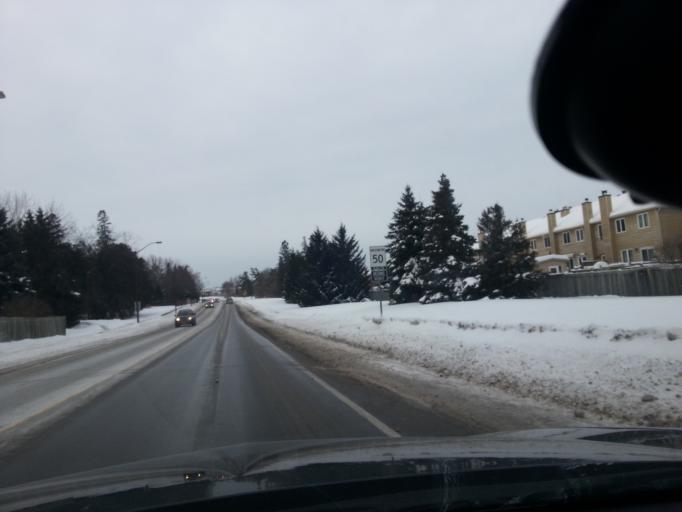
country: CA
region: Ontario
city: Bells Corners
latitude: 45.3068
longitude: -75.9021
